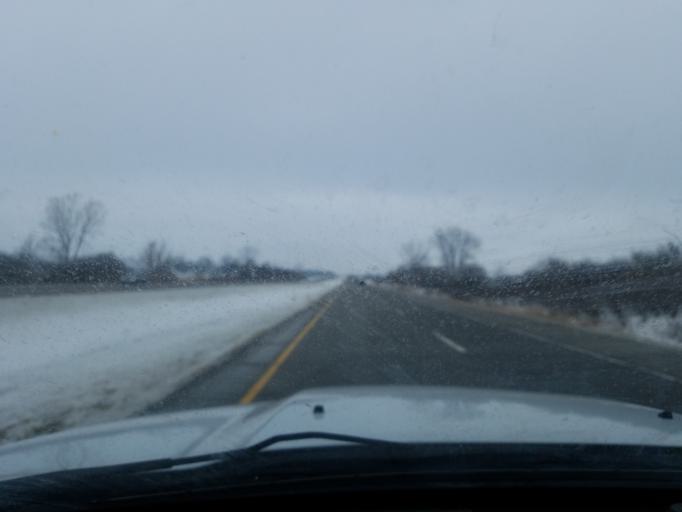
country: US
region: Indiana
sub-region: Marshall County
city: Argos
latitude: 41.2260
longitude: -86.2610
